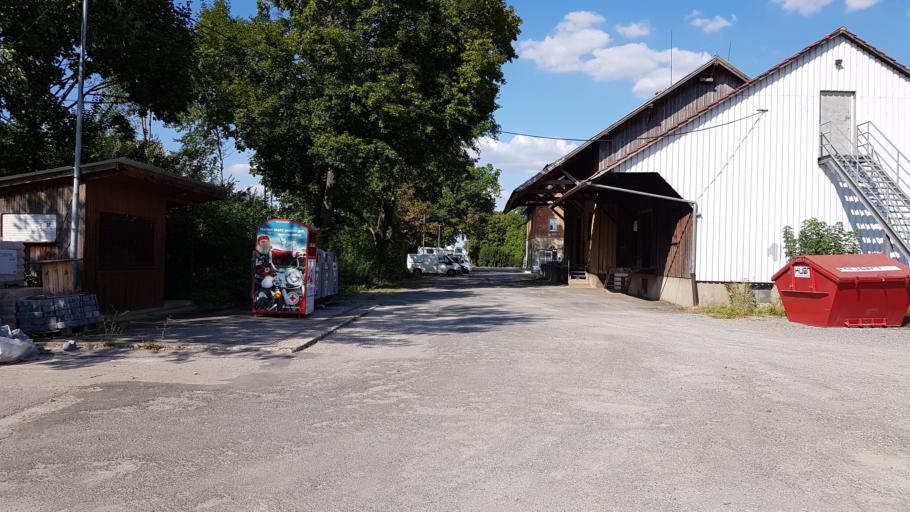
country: DE
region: Baden-Wuerttemberg
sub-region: Regierungsbezirk Stuttgart
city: Bondorf
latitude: 48.4886
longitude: 8.8088
